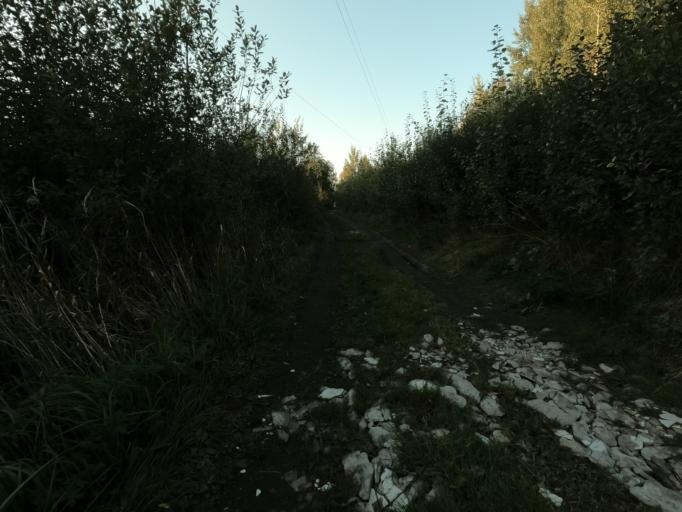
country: RU
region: Leningrad
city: Nikol'skoye
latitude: 59.7143
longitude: 30.7971
